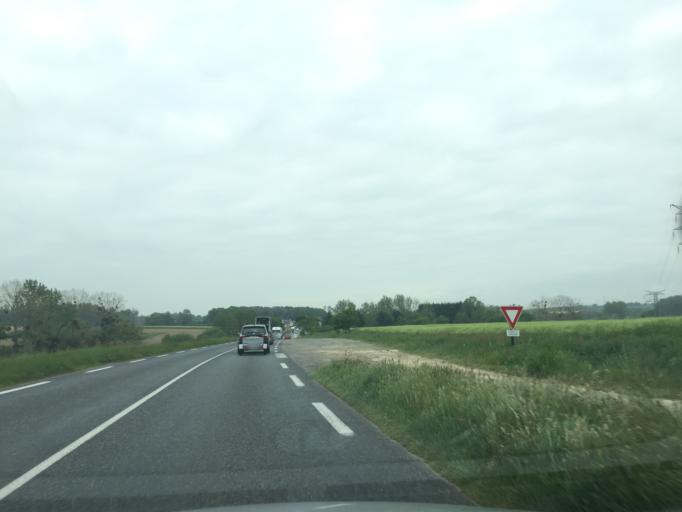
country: FR
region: Brittany
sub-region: Departement des Cotes-d'Armor
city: Lamballe
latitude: 48.5060
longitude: -2.4567
